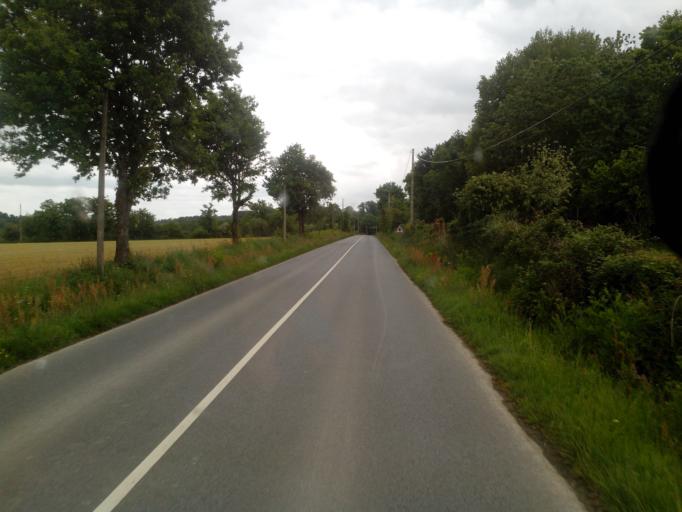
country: FR
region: Brittany
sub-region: Departement d'Ille-et-Vilaine
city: Chasne-sur-Illet
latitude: 48.2408
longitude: -1.5508
